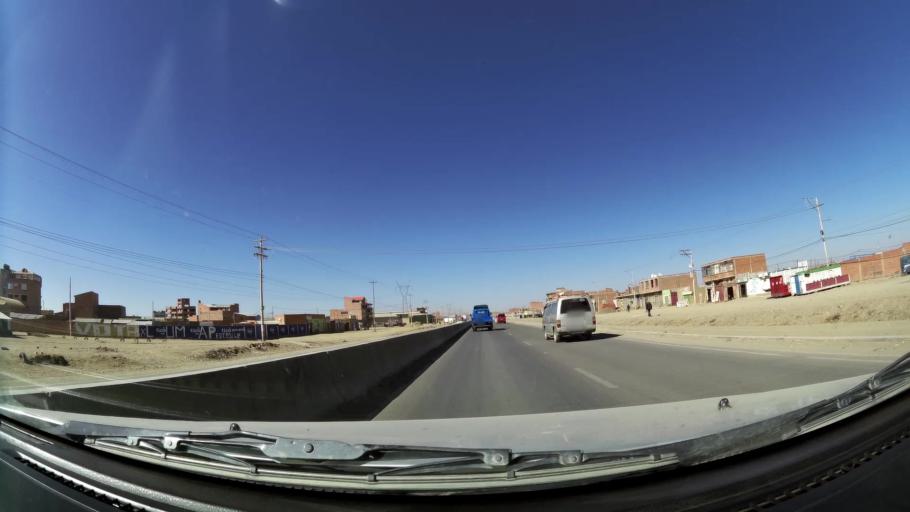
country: BO
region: La Paz
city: La Paz
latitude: -16.6028
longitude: -68.1835
